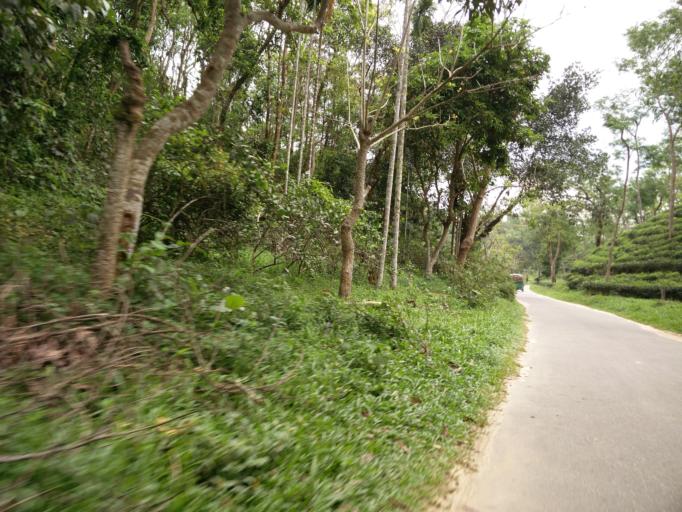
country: IN
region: Tripura
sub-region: Dhalai
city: Kamalpur
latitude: 24.3025
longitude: 91.7890
